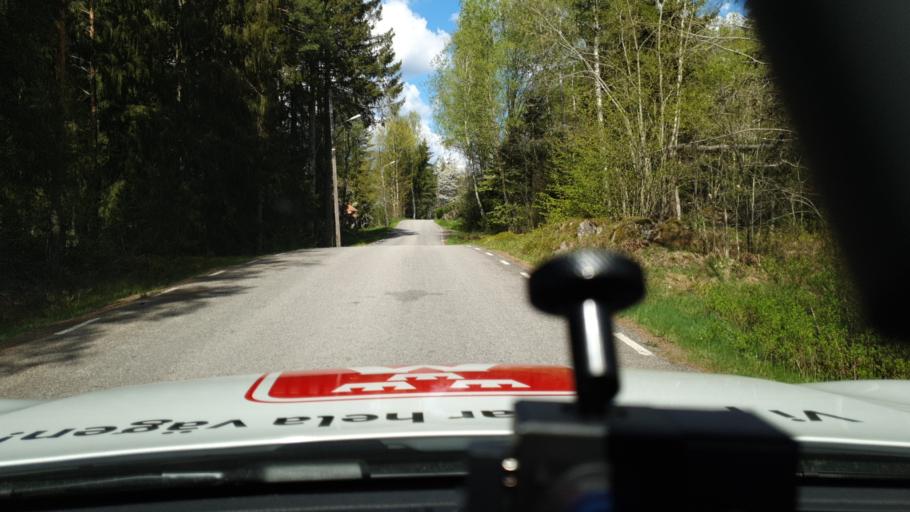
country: SE
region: Kalmar
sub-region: Vasterviks Kommun
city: Ankarsrum
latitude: 57.7821
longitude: 16.1478
